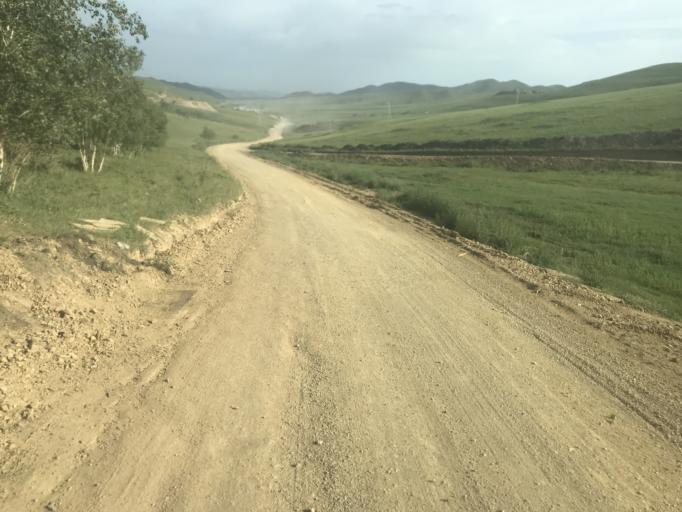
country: MN
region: Central Aimak
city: Javhlant
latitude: 48.7271
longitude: 106.1358
